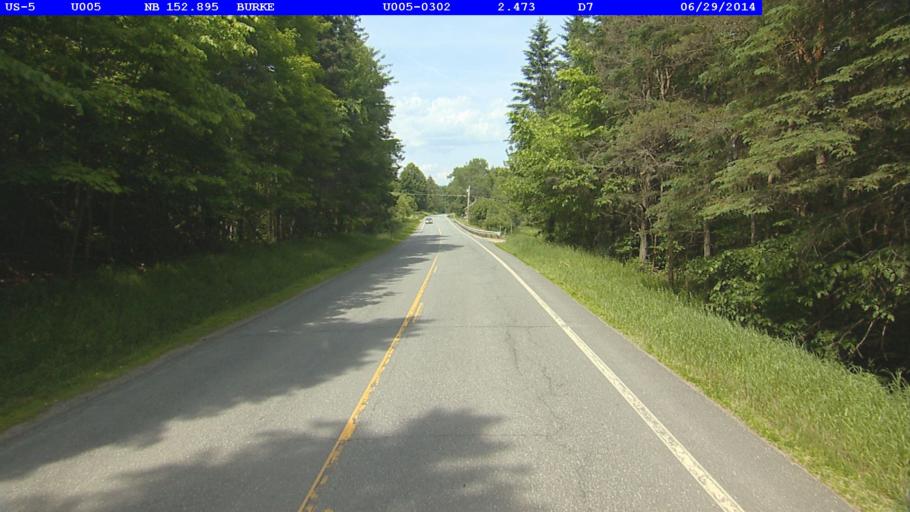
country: US
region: Vermont
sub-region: Caledonia County
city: Lyndonville
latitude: 44.6203
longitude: -71.9717
